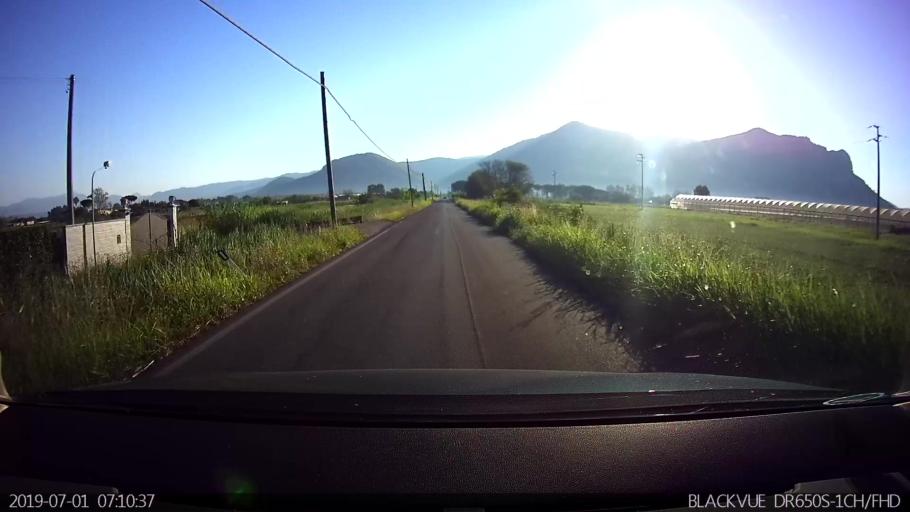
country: IT
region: Latium
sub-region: Provincia di Latina
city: Borgo Hermada
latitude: 41.3137
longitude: 13.1725
